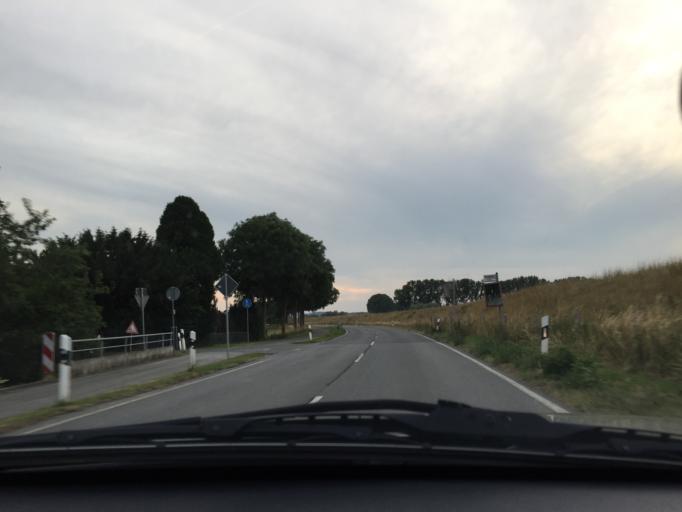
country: DE
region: North Rhine-Westphalia
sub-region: Regierungsbezirk Dusseldorf
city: Kleve
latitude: 51.7883
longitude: 6.1998
